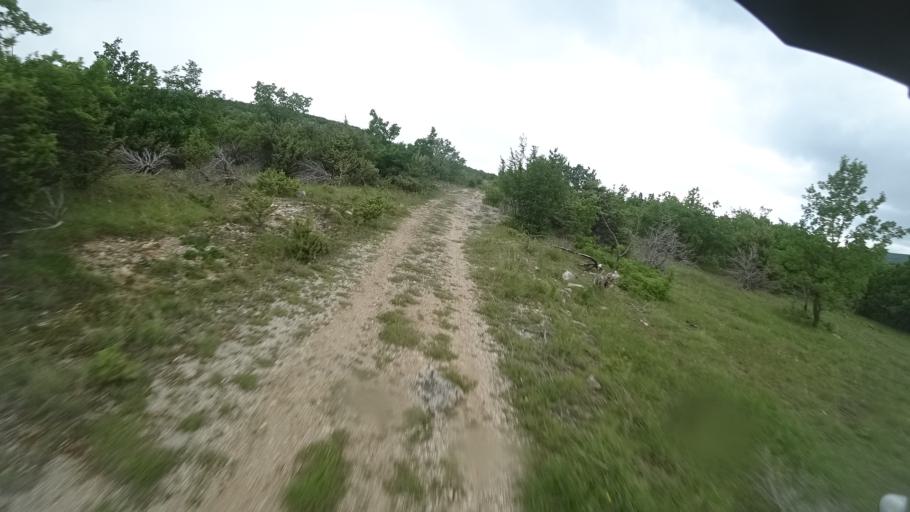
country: HR
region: Sibensko-Kniniska
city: Knin
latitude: 44.0284
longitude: 16.2575
